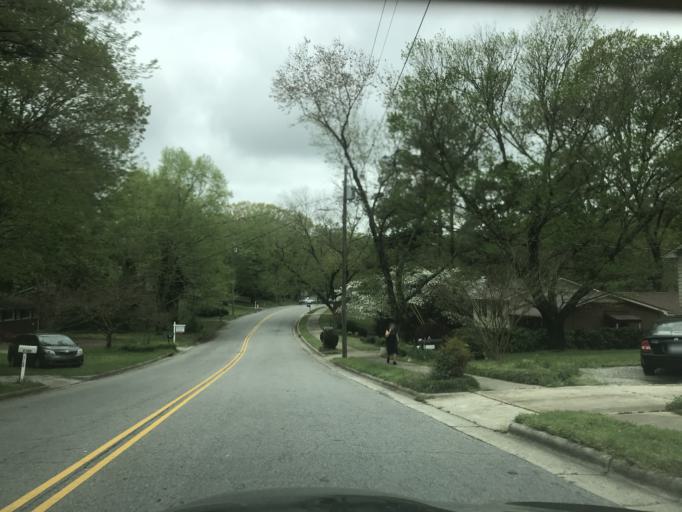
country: US
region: North Carolina
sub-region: Wake County
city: West Raleigh
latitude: 35.7513
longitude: -78.6712
